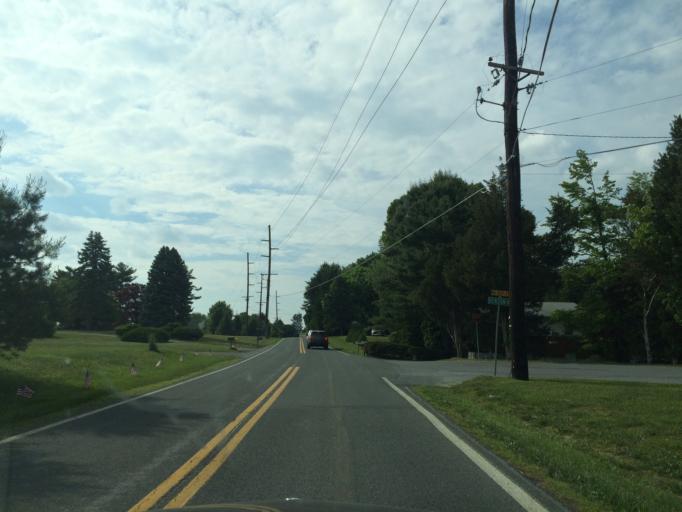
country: US
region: Maryland
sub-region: Baltimore County
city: Reisterstown
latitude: 39.4653
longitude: -76.8985
